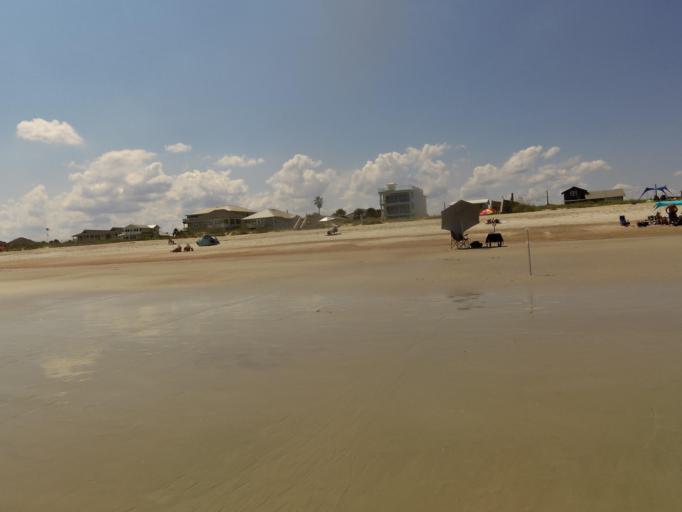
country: US
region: Florida
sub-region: Nassau County
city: Fernandina Beach
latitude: 30.6647
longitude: -81.4304
